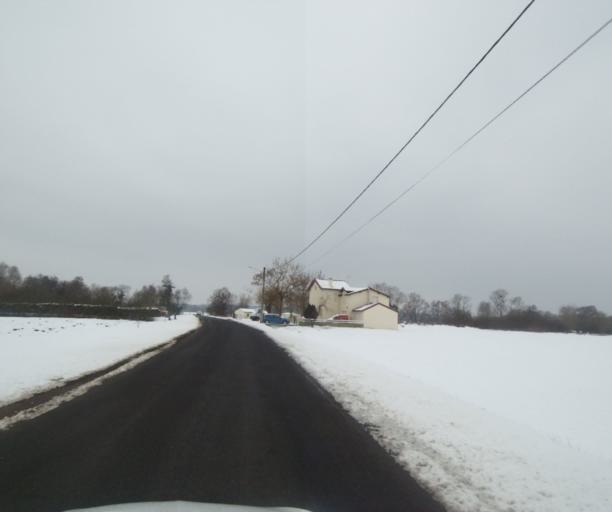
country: FR
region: Champagne-Ardenne
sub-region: Departement de la Haute-Marne
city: Saint-Dizier
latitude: 48.5783
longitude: 4.8939
